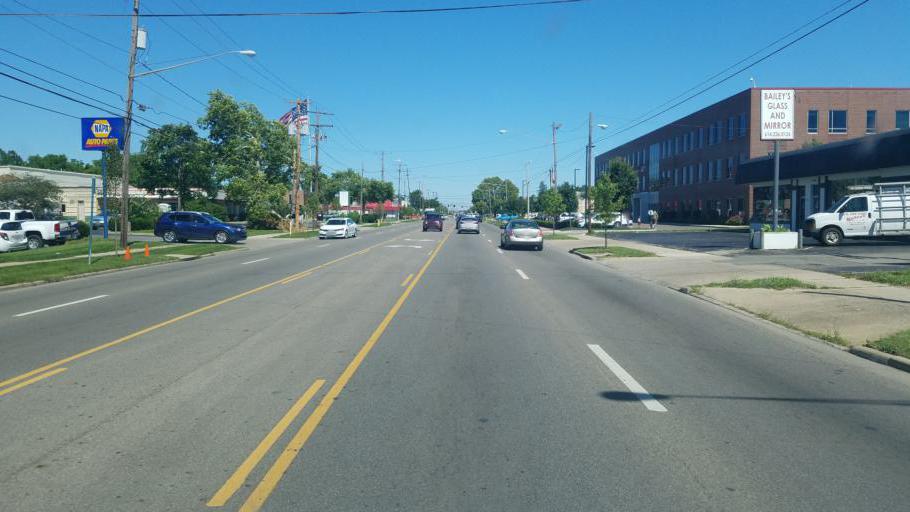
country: US
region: Ohio
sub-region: Franklin County
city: Whitehall
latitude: 39.9559
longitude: -82.8913
